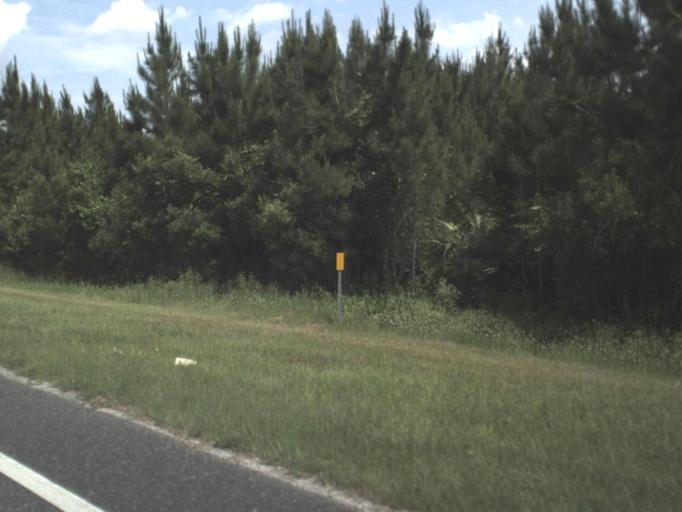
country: US
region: Florida
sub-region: Putnam County
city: Palatka
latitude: 29.6311
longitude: -81.7391
